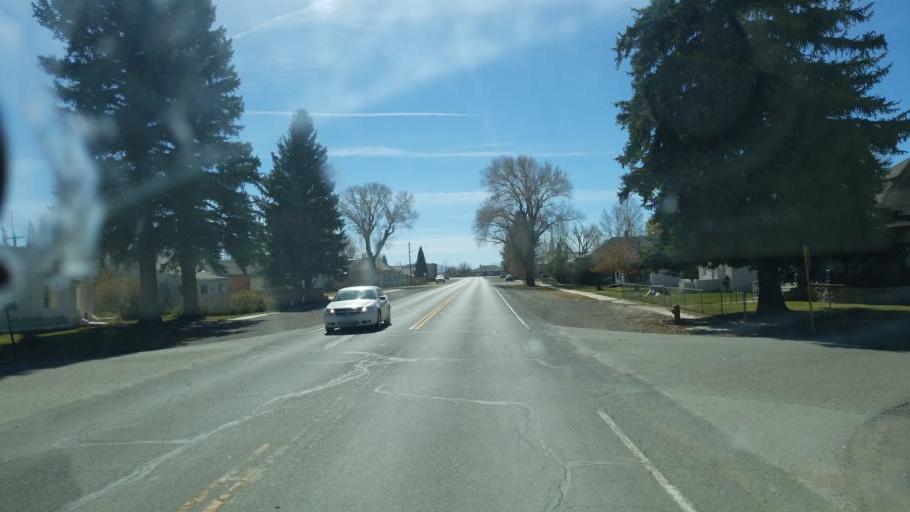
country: US
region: Colorado
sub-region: Conejos County
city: Conejos
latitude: 37.2718
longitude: -105.9600
